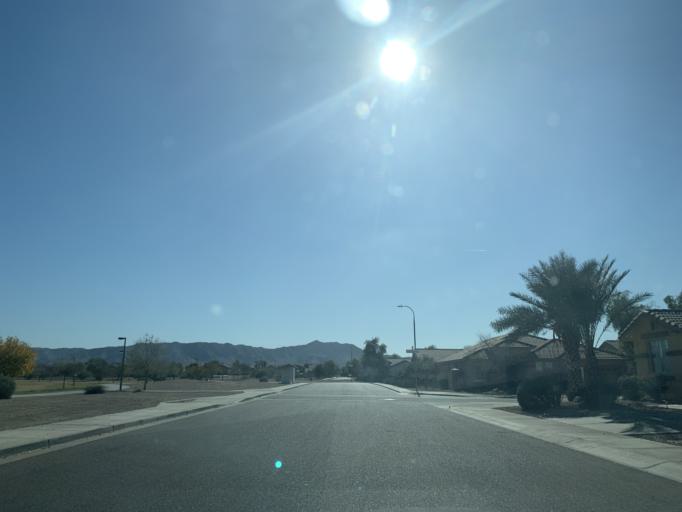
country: US
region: Arizona
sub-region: Maricopa County
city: Laveen
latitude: 33.3986
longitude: -112.1294
